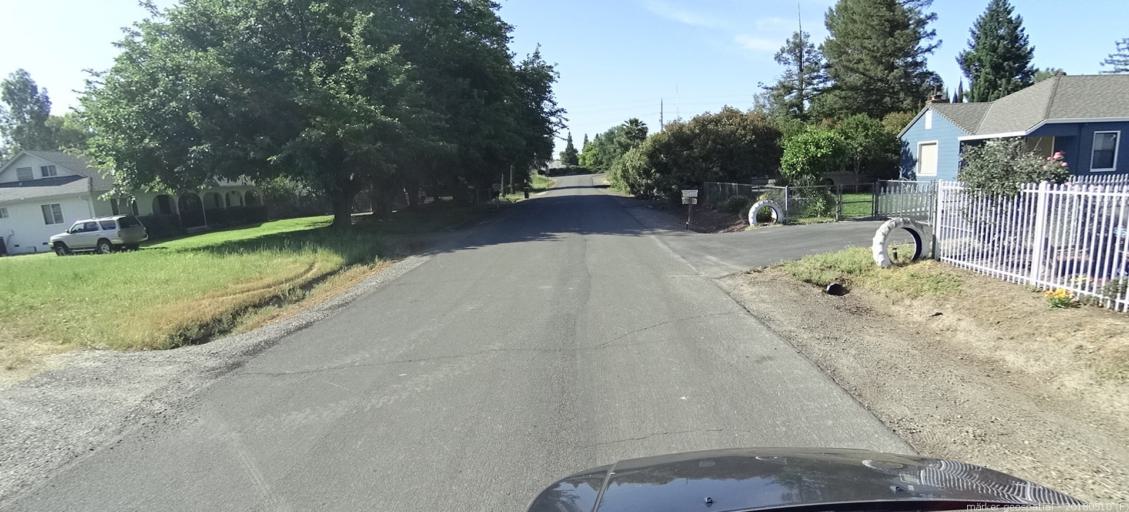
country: US
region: California
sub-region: Sacramento County
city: Rio Linda
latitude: 38.6578
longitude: -121.4779
